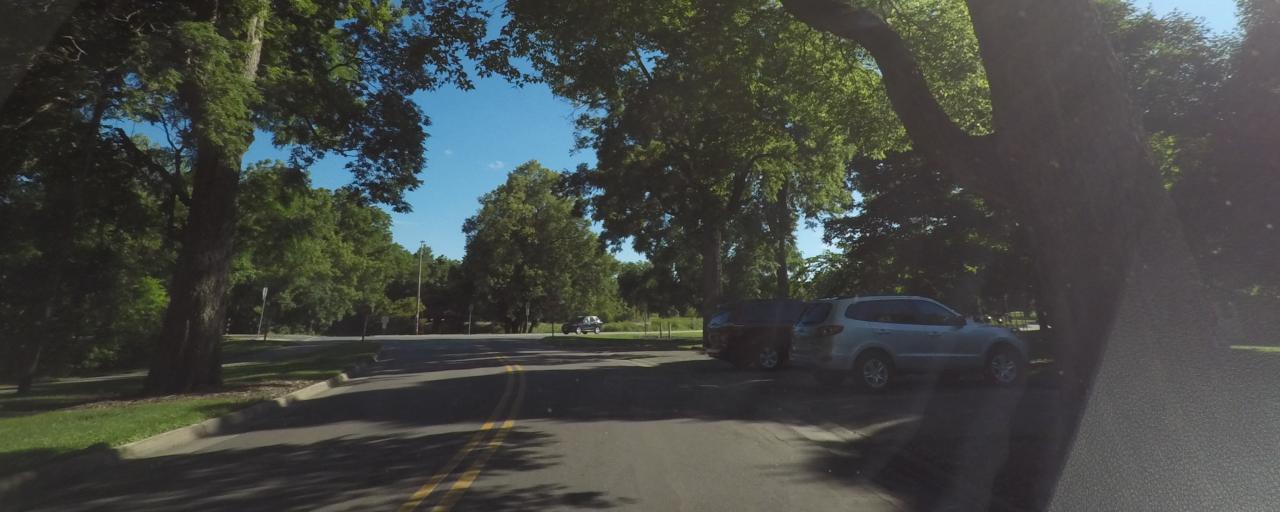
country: US
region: Wisconsin
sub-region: Rock County
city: Janesville
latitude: 42.6770
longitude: -88.9911
